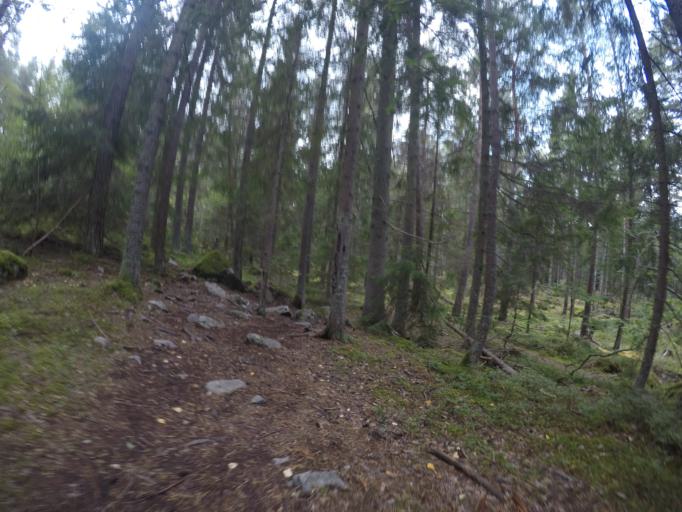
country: SE
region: Vaestmanland
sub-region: Vasteras
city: Vasteras
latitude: 59.6470
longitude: 16.5200
